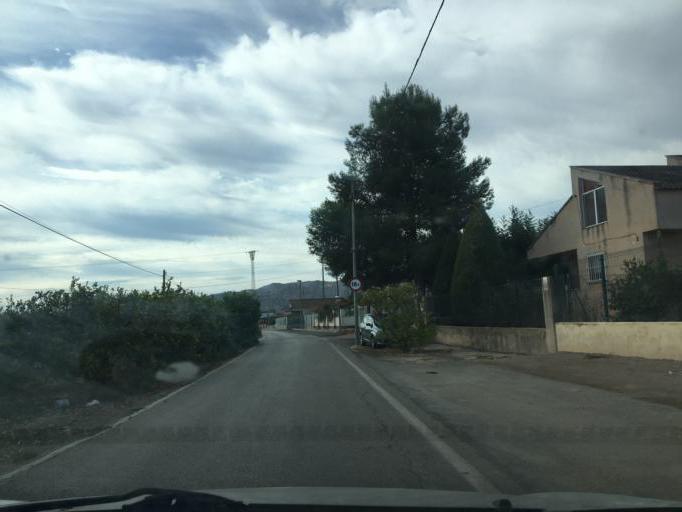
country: ES
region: Murcia
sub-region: Murcia
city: Santomera
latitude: 38.0153
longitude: -1.0462
